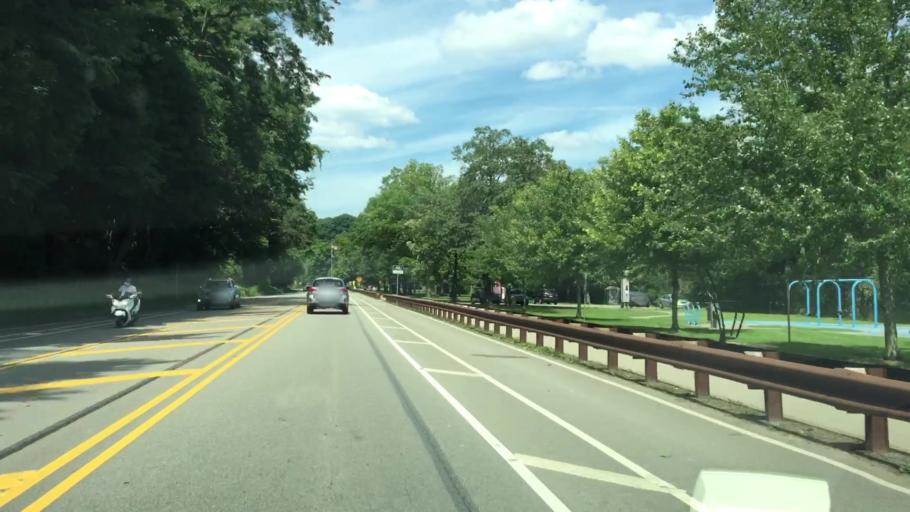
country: US
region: Pennsylvania
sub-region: Allegheny County
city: South Park Township
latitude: 40.3162
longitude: -80.0066
